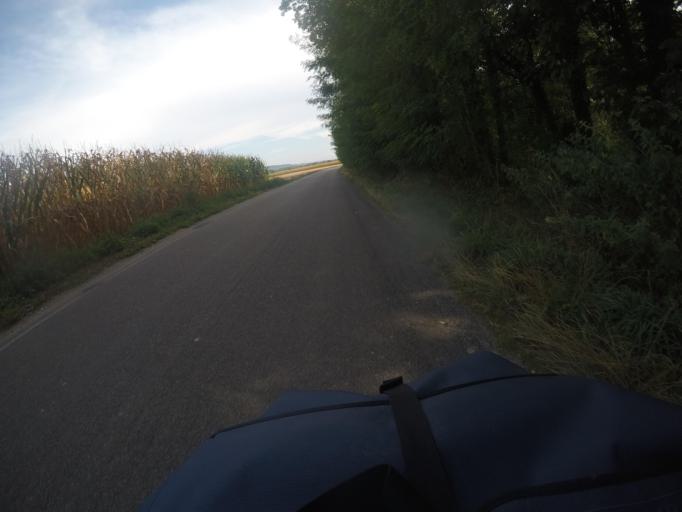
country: DE
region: Baden-Wuerttemberg
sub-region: Freiburg Region
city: Efringen-Kirchen
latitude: 47.6403
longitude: 7.5690
